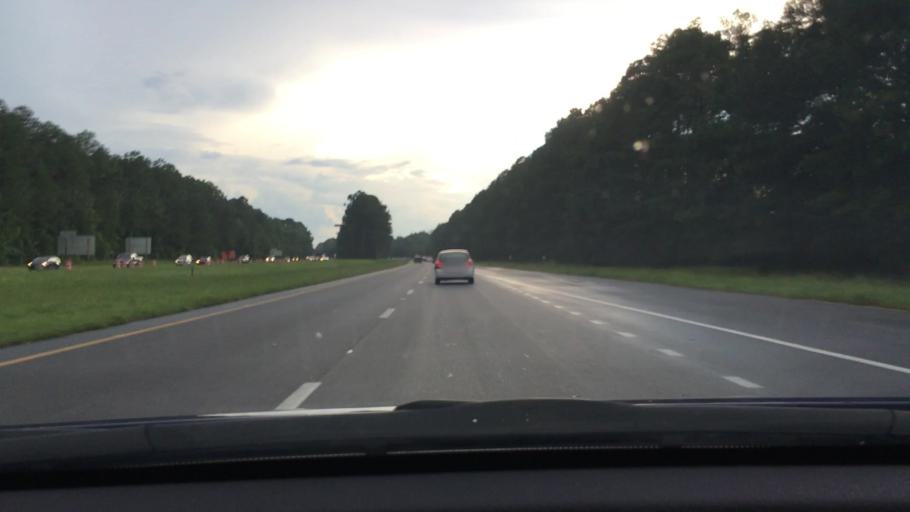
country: US
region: South Carolina
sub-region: Lee County
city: Bishopville
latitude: 34.1955
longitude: -80.2870
